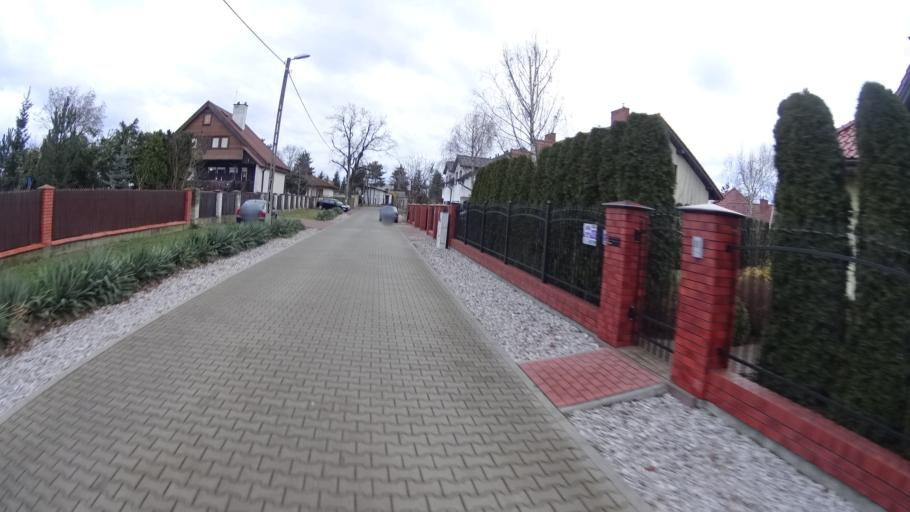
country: PL
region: Masovian Voivodeship
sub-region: Powiat pruszkowski
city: Granica
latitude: 52.1462
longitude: 20.7950
